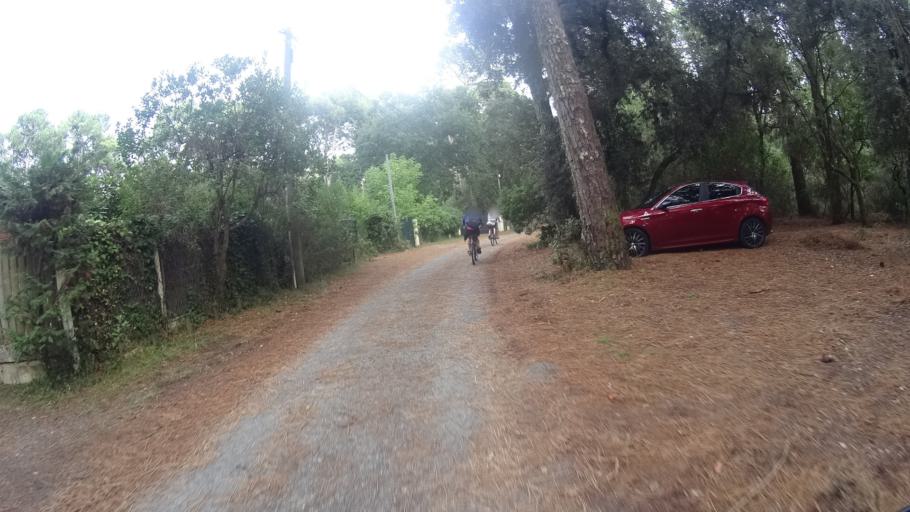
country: FR
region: Aquitaine
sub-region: Departement de la Gironde
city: Lacanau
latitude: 44.9900
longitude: -1.1405
